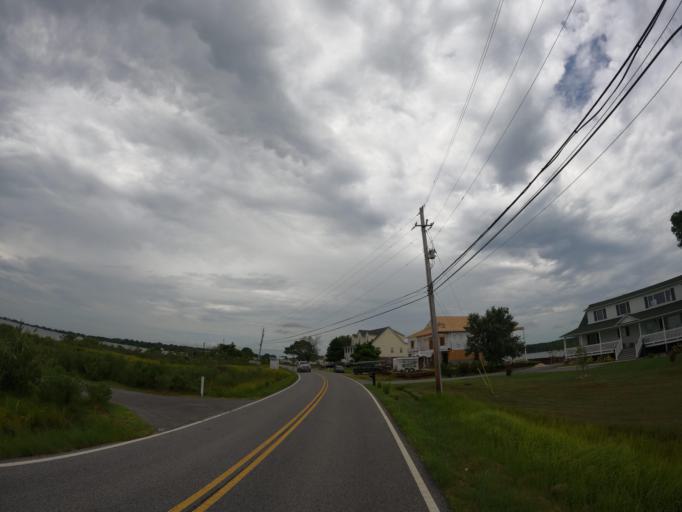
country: US
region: Maryland
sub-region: Saint Mary's County
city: Lexington Park
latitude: 38.1341
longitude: -76.4966
